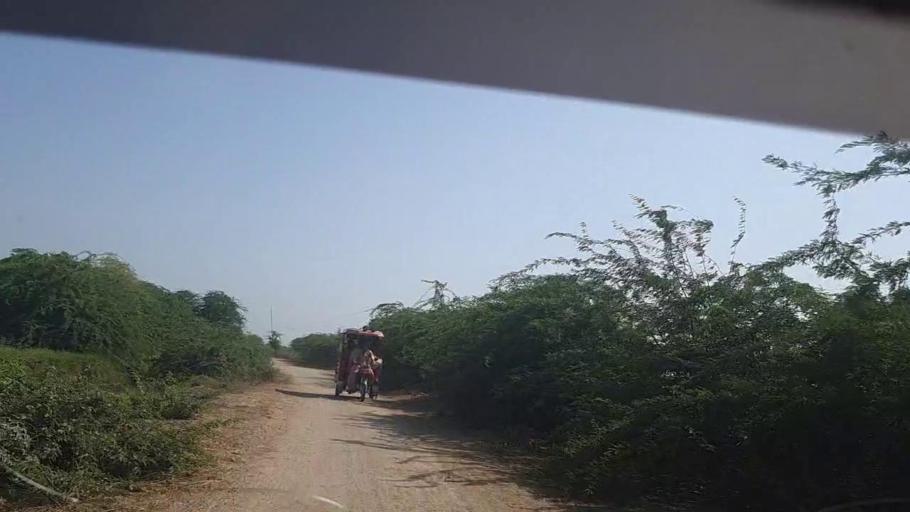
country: PK
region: Sindh
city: Rajo Khanani
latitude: 24.9625
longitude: 68.8915
